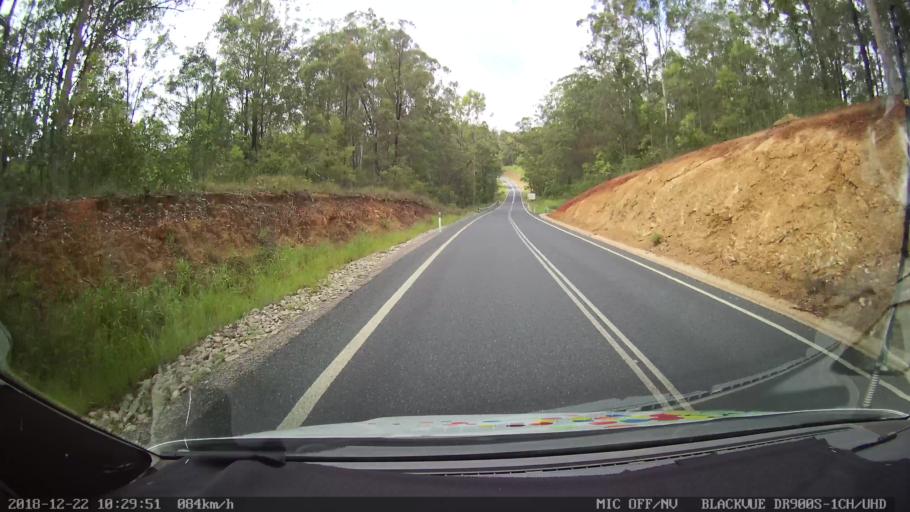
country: AU
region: New South Wales
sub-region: Clarence Valley
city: South Grafton
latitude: -29.6146
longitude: 152.6082
